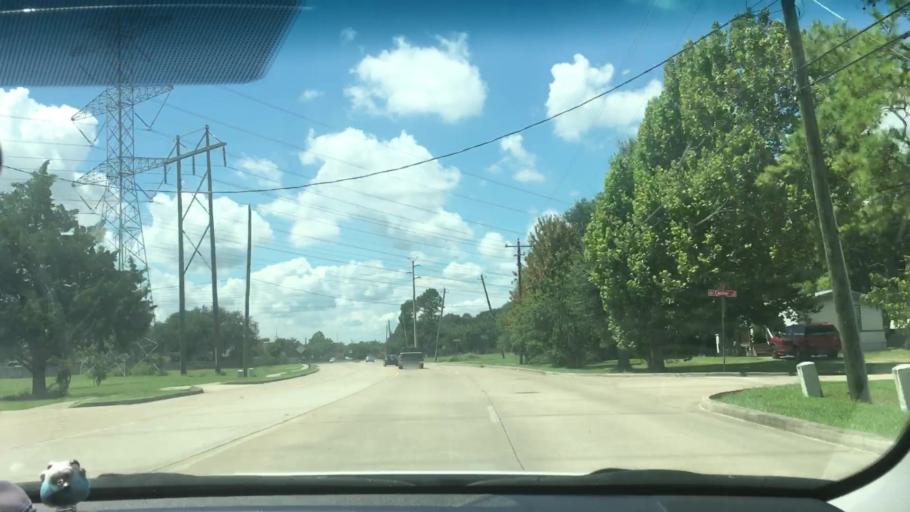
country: US
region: Texas
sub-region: Fort Bend County
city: Missouri City
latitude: 29.6099
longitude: -95.5437
